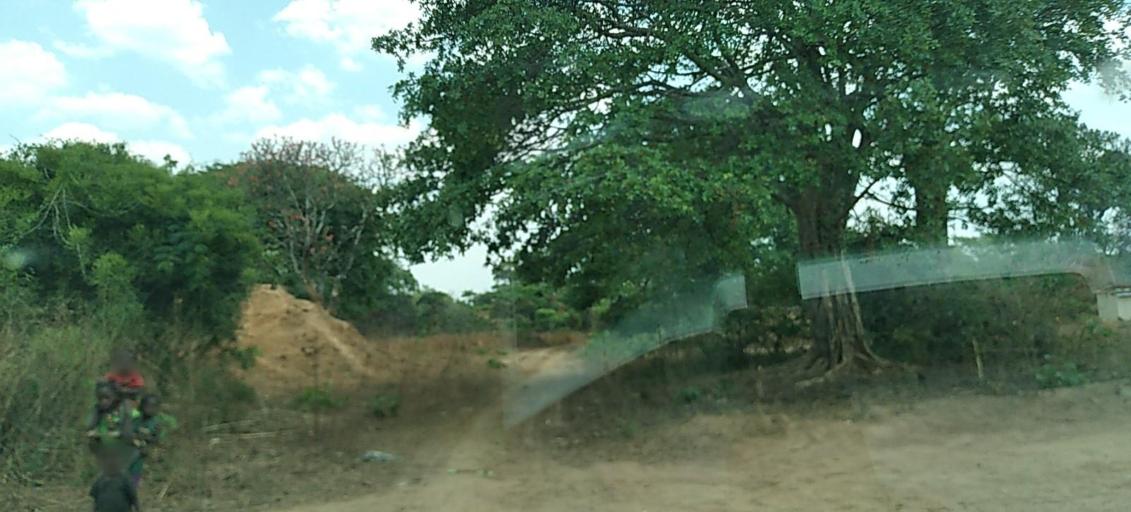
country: CD
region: Katanga
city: Kipushi
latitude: -12.0393
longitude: 27.4379
